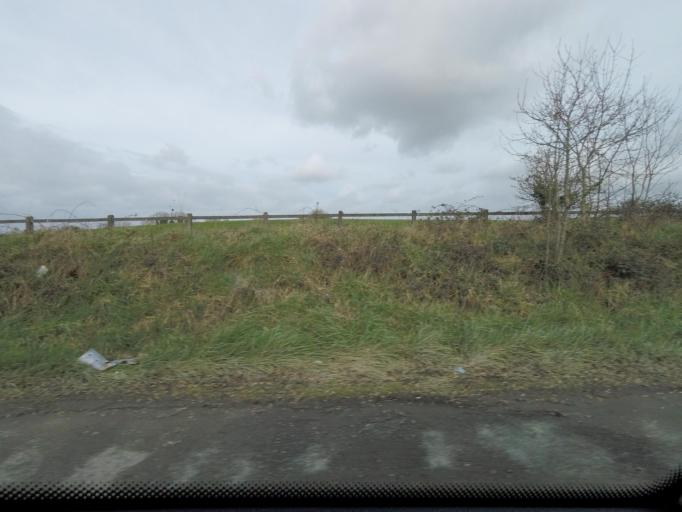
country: IE
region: Leinster
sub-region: Kildare
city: Naas
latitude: 53.2073
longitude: -6.6361
